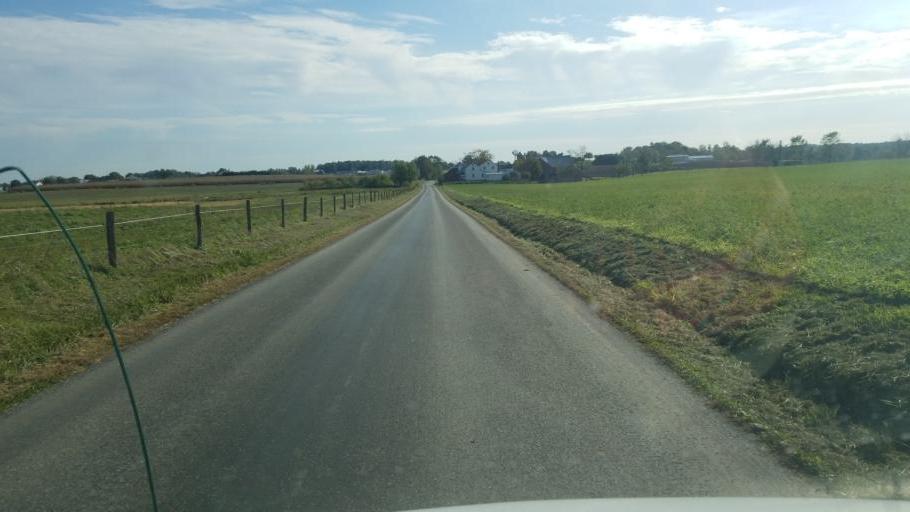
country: US
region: Ohio
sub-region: Wayne County
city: Apple Creek
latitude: 40.7362
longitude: -81.7879
